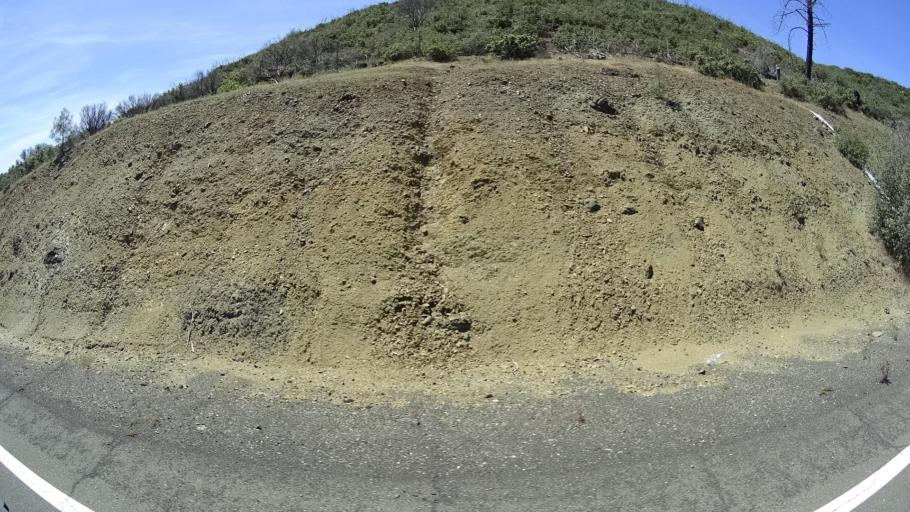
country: US
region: California
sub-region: Lake County
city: Hidden Valley Lake
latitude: 38.7311
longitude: -122.5220
